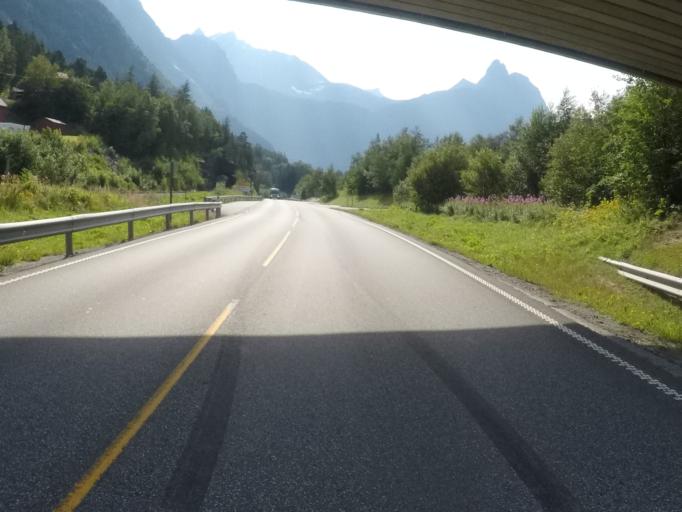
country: NO
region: More og Romsdal
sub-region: Rauma
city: Andalsnes
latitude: 62.5401
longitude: 7.7232
